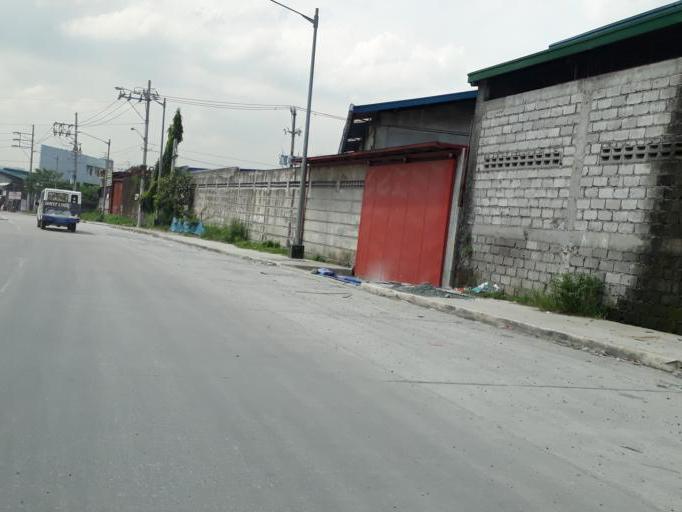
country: PH
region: Calabarzon
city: Bagong Pagasa
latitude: 14.7053
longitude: 121.0137
